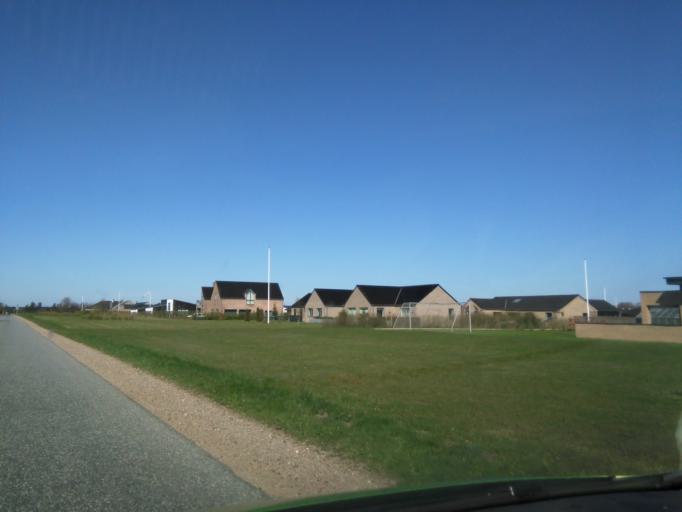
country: DK
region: South Denmark
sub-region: Billund Kommune
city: Billund
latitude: 55.7093
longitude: 9.1205
